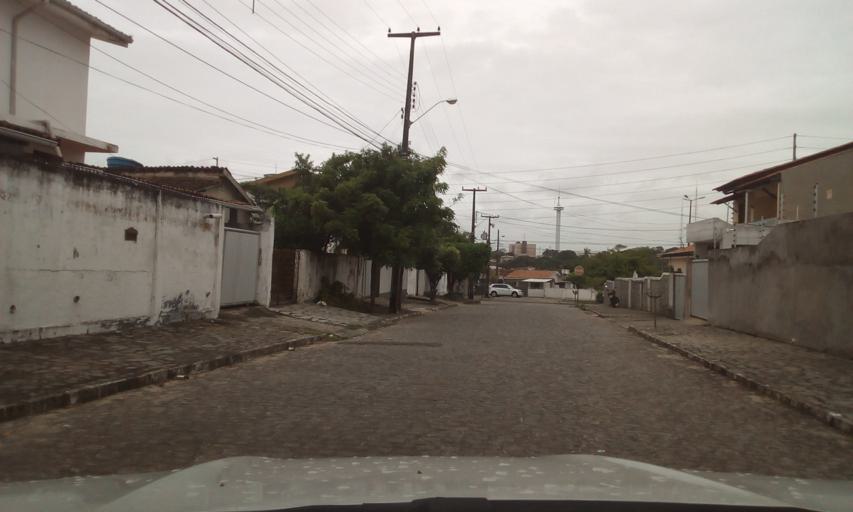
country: BR
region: Paraiba
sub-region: Joao Pessoa
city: Joao Pessoa
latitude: -7.1092
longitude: -34.8684
